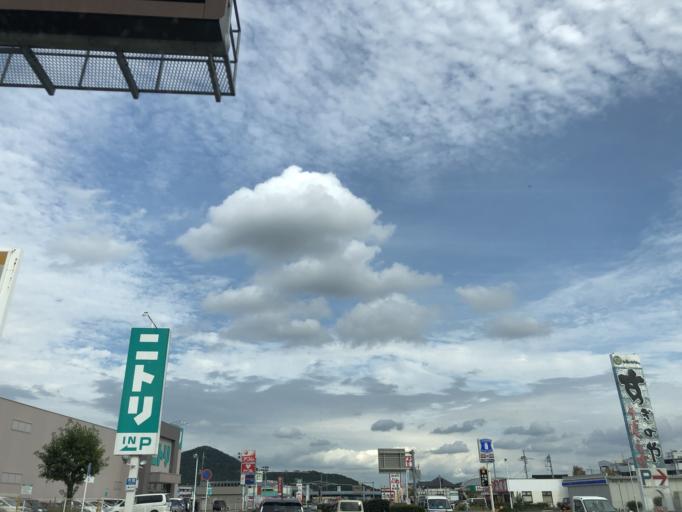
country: JP
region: Tochigi
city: Sano
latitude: 36.2963
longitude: 139.6002
